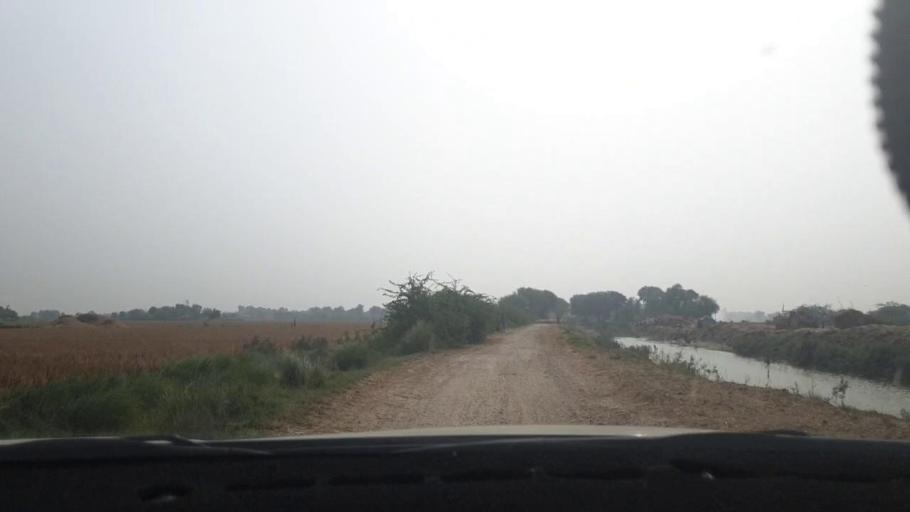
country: PK
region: Sindh
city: Tando Muhammad Khan
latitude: 25.0651
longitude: 68.5070
